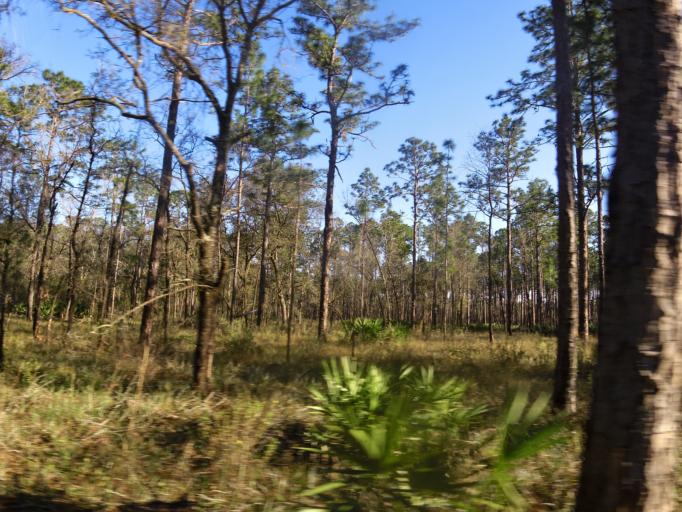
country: US
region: Florida
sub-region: Clay County
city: Middleburg
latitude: 30.1487
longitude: -81.8944
